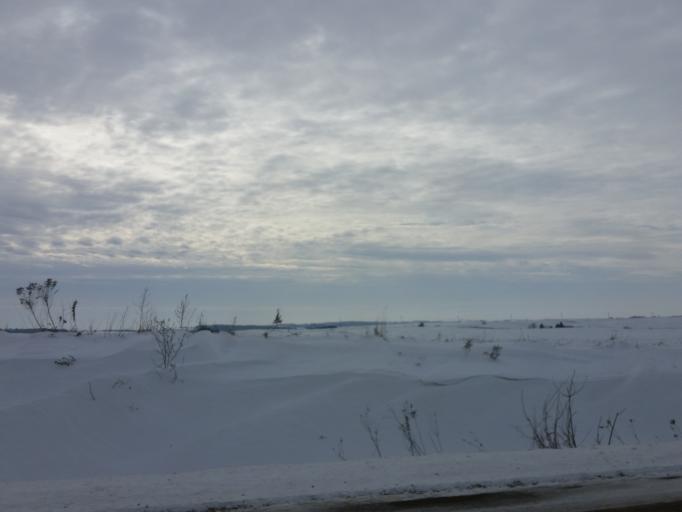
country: US
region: Iowa
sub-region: Dubuque County
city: Peosta
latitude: 42.3821
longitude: -90.7503
